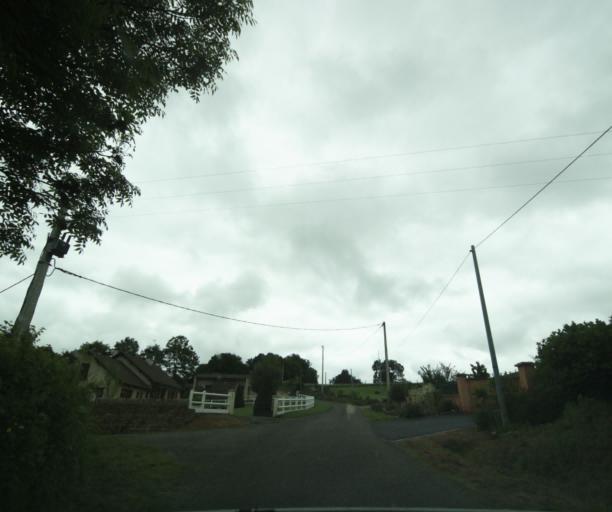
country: FR
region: Bourgogne
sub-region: Departement de Saone-et-Loire
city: Charolles
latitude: 46.4713
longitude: 4.3300
